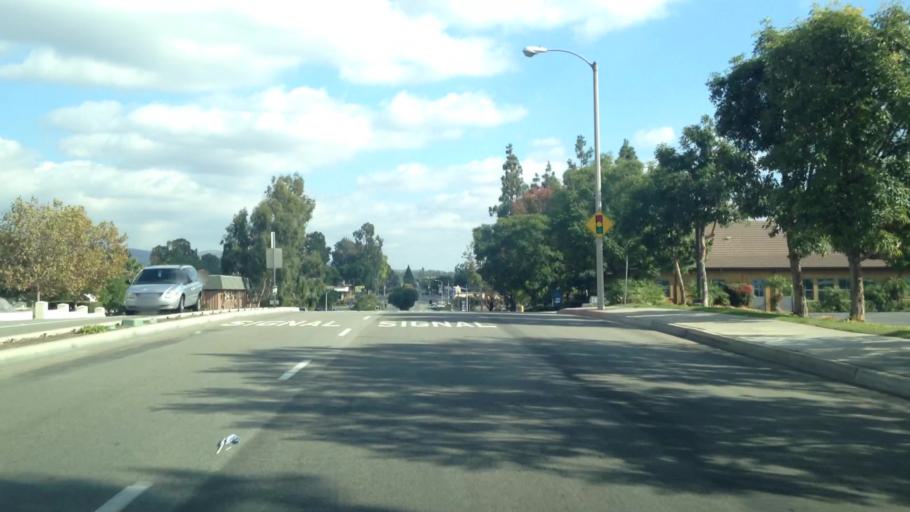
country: US
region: California
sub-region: Orange County
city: Yorba Linda
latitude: 33.8884
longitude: -117.8310
